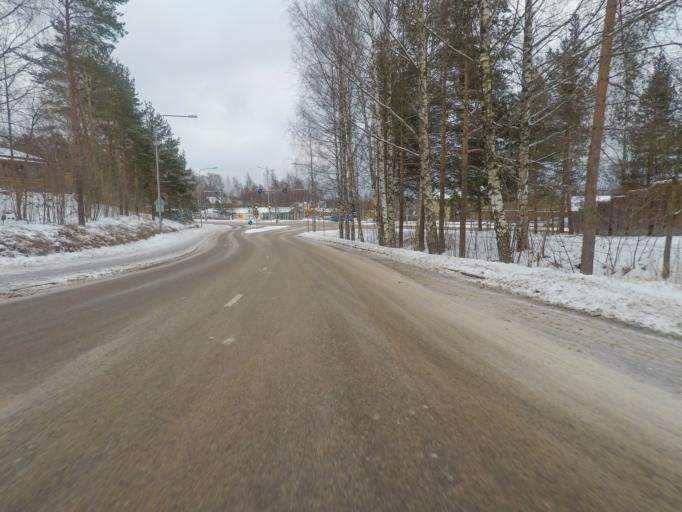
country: FI
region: Uusimaa
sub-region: Helsinki
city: Vantaa
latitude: 60.2216
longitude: 25.1079
